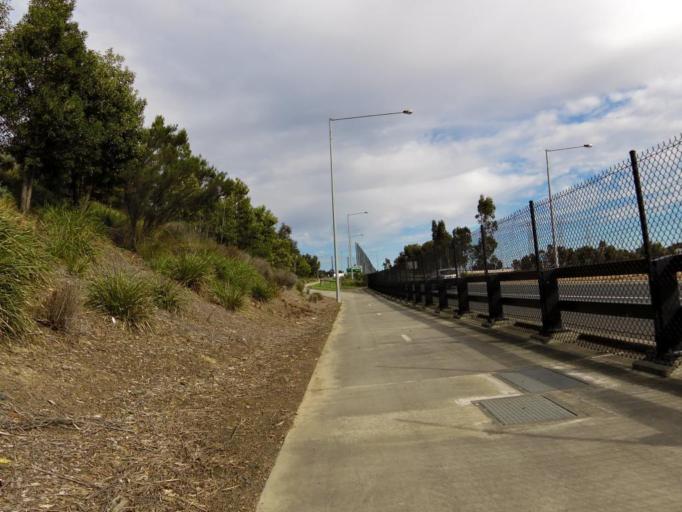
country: AU
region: Victoria
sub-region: Knox
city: Wantirna
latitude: -37.8298
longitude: 145.2180
